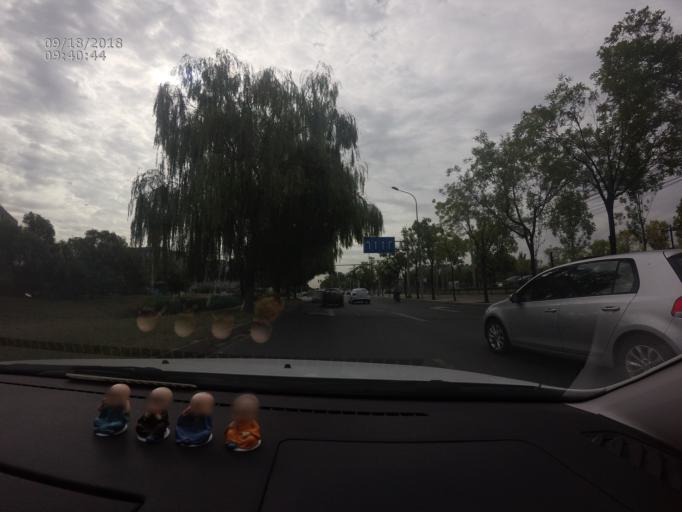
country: CN
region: Beijing
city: Xibeiwang
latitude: 40.0673
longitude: 116.2401
